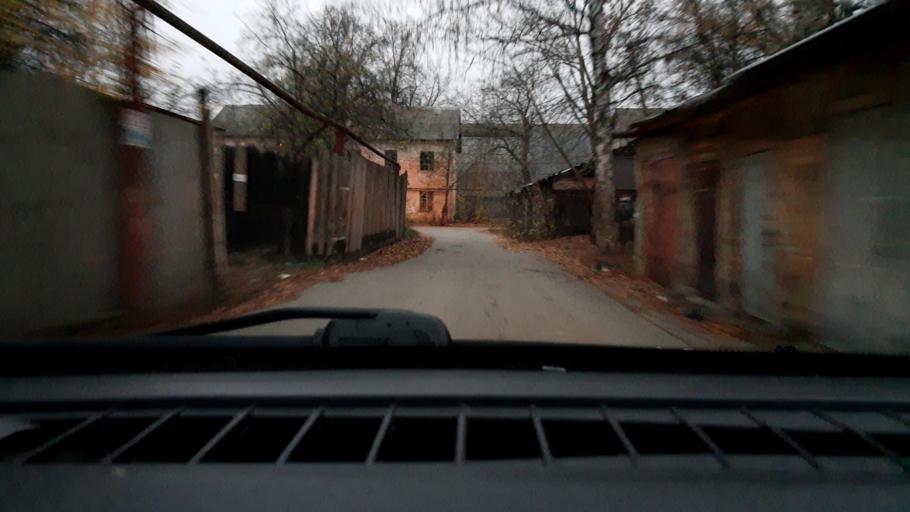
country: RU
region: Nizjnij Novgorod
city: Nizhniy Novgorod
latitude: 56.2618
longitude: 43.9304
